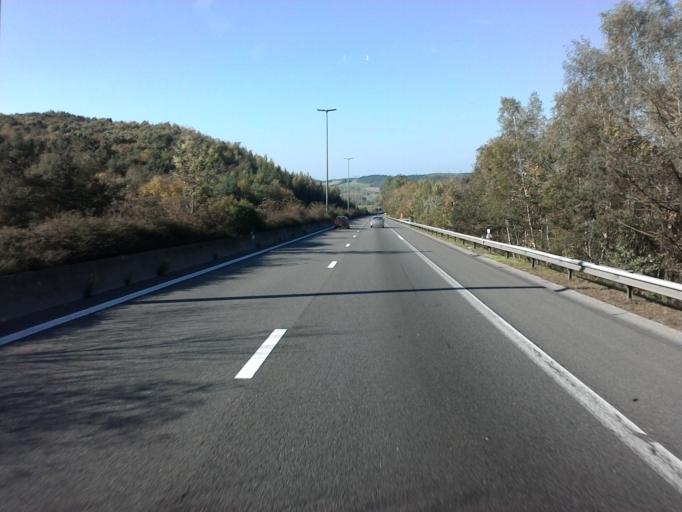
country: BE
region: Wallonia
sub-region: Province du Luxembourg
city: Tellin
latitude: 50.0765
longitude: 5.1767
